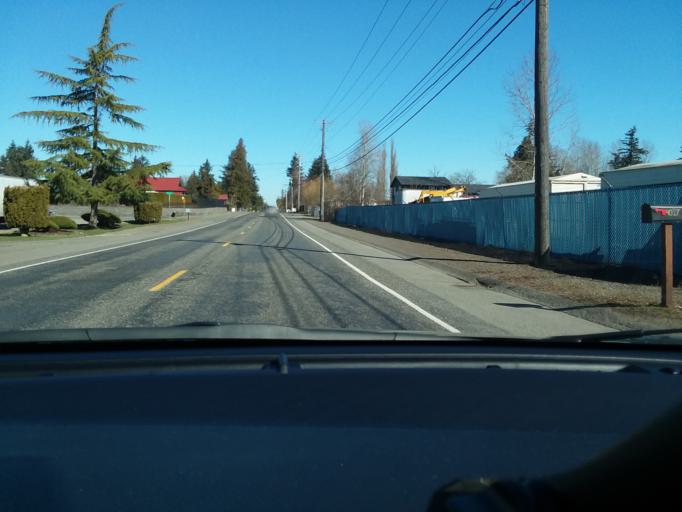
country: US
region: Washington
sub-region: Pierce County
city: Midland
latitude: 47.1748
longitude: -122.3890
